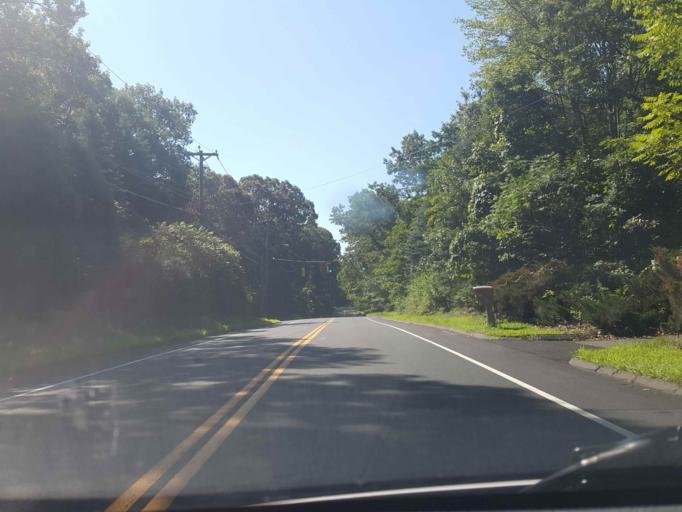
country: US
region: Connecticut
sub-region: New Haven County
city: Guilford
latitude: 41.3188
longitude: -72.6983
